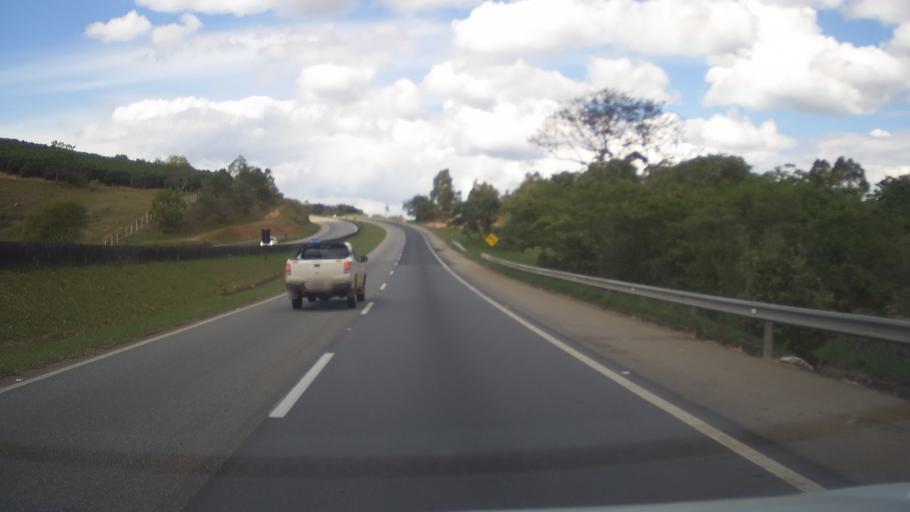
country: BR
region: Minas Gerais
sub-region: Santo Antonio Do Amparo
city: Santo Antonio do Amparo
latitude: -20.8451
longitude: -44.8300
